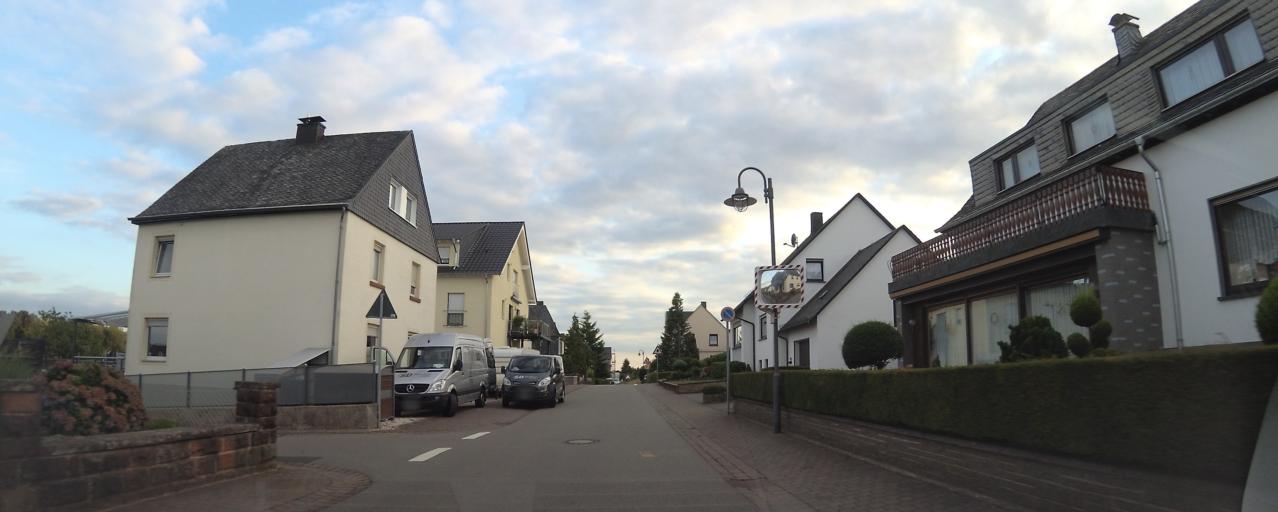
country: DE
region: Rheinland-Pfalz
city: Fohren
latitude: 49.8642
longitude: 6.7704
